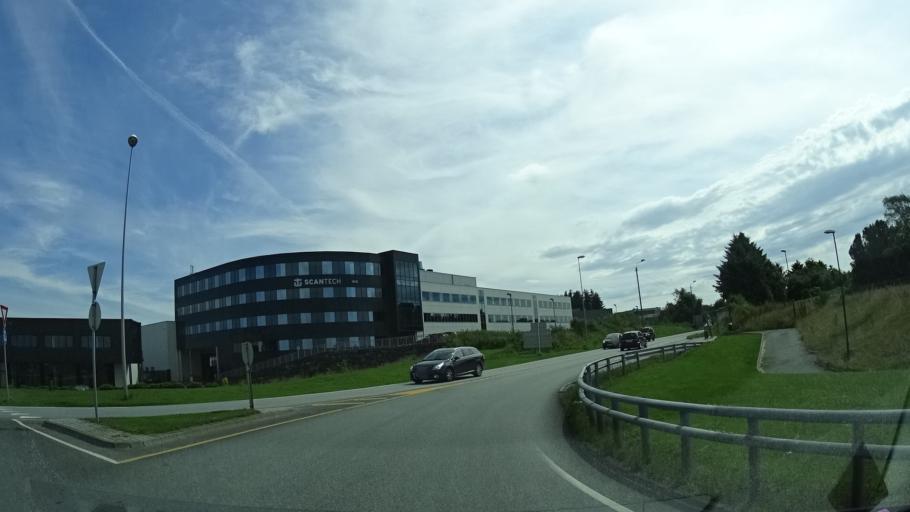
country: NO
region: Rogaland
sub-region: Randaberg
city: Randaberg
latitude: 58.9948
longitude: 5.6510
